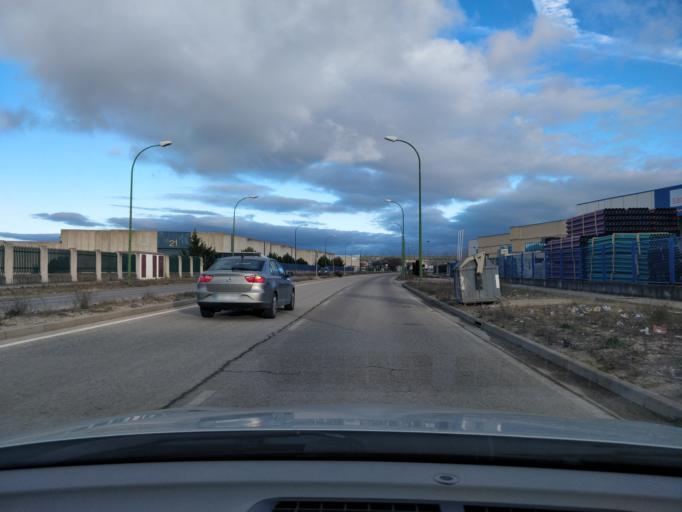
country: ES
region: Castille and Leon
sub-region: Provincia de Burgos
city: Sotragero
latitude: 42.3704
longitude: -3.7227
